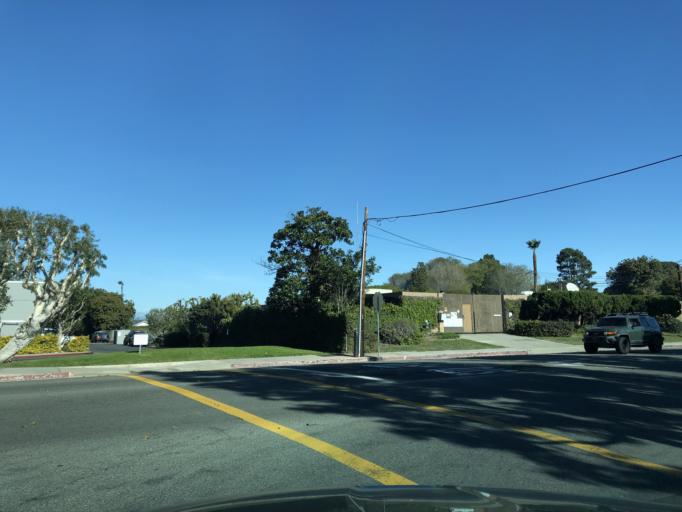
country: US
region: California
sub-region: Orange County
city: Westminster
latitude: 33.7224
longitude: -118.0501
